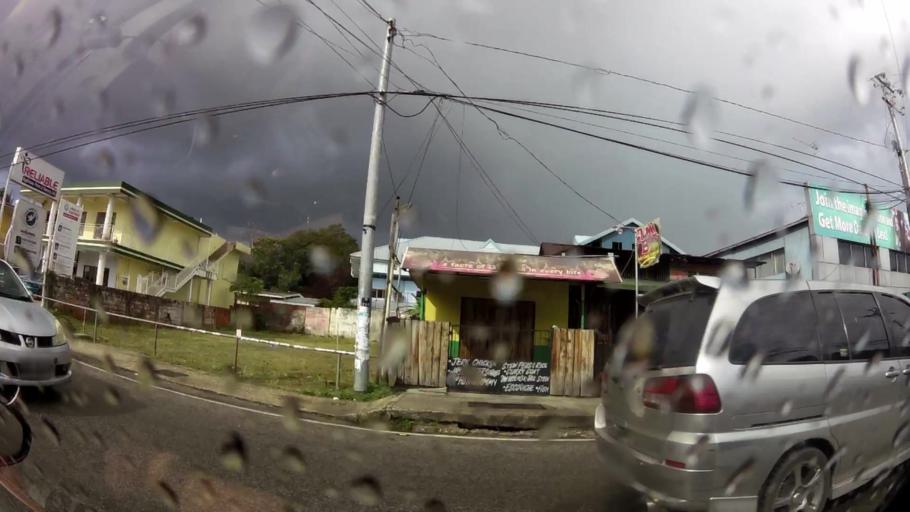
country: TT
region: Tunapuna/Piarco
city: Tunapuna
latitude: 10.6472
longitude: -61.4021
